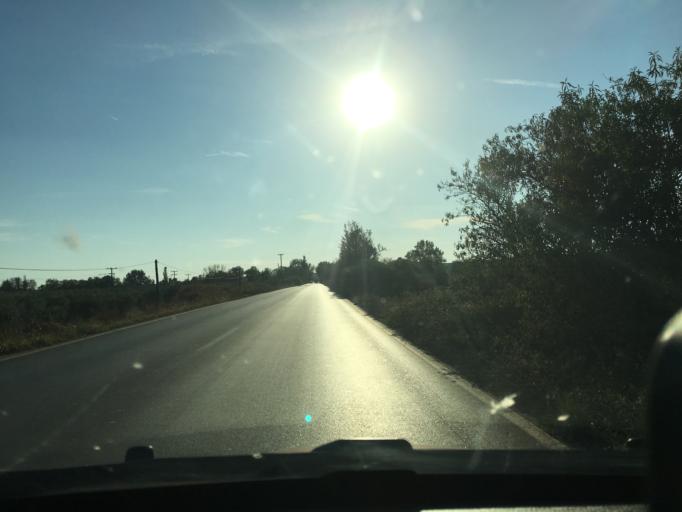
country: GR
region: Central Macedonia
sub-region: Nomos Chalkidikis
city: Olynthos
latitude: 40.2819
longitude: 23.3594
